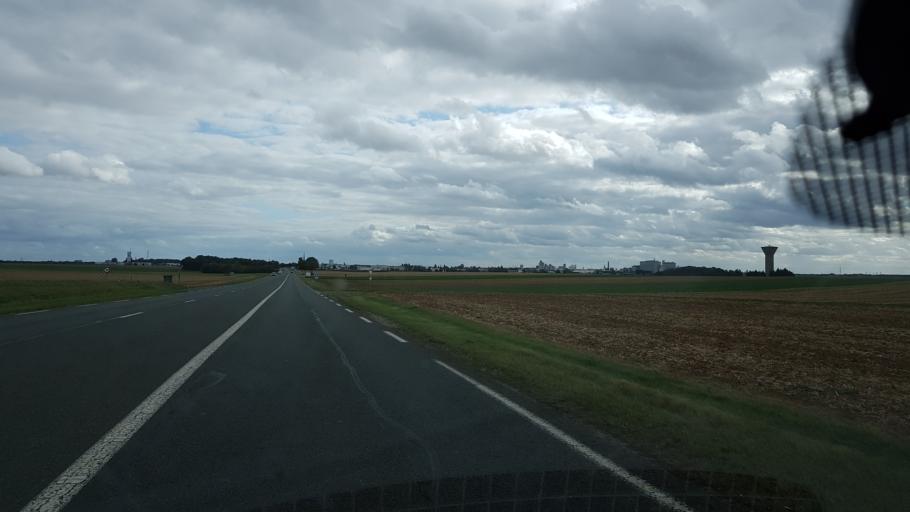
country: FR
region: Centre
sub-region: Departement du Loiret
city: Pithiviers
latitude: 48.1970
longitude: 2.2422
